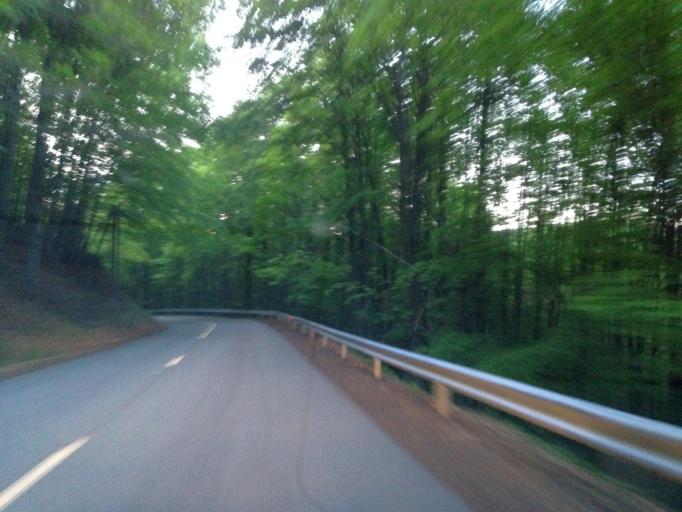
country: HU
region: Nograd
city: Batonyterenye
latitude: 47.9014
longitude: 19.8844
